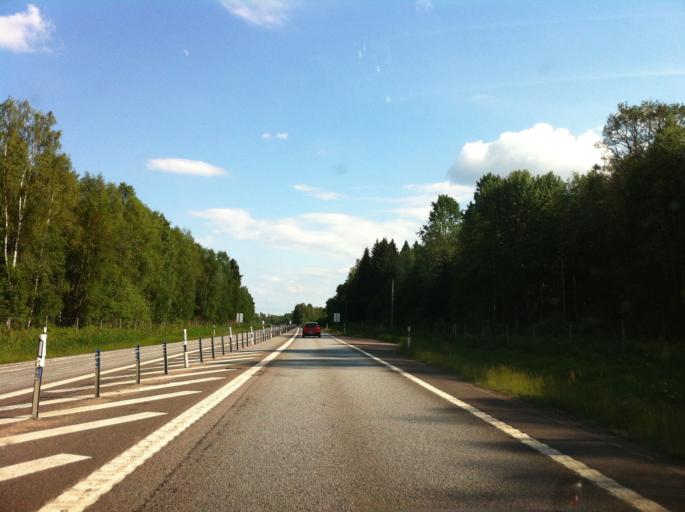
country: SE
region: Vaermland
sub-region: Kils Kommun
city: Kil
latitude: 59.4507
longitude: 13.3755
